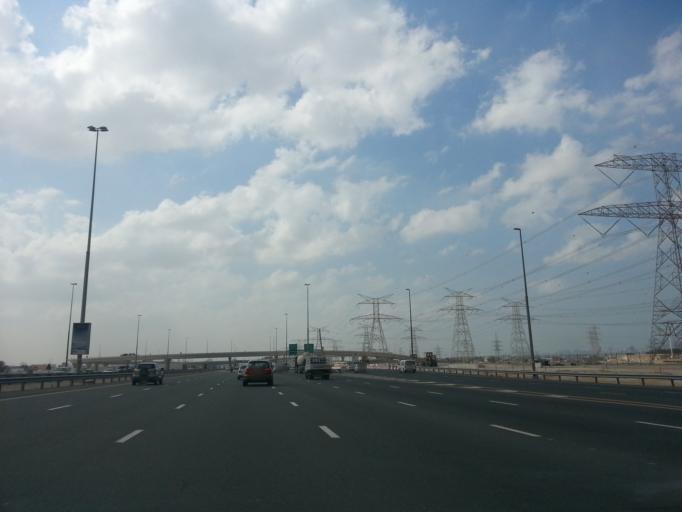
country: AE
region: Dubai
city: Dubai
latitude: 25.1072
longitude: 55.2373
